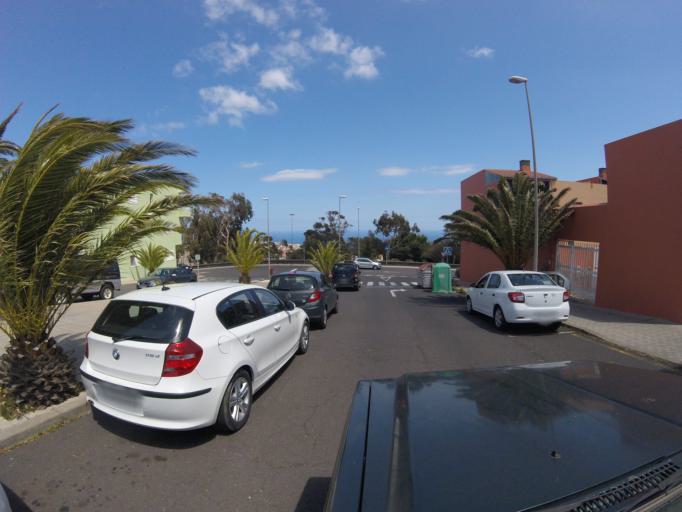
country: ES
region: Canary Islands
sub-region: Provincia de Santa Cruz de Tenerife
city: La Laguna
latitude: 28.4437
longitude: -16.3105
